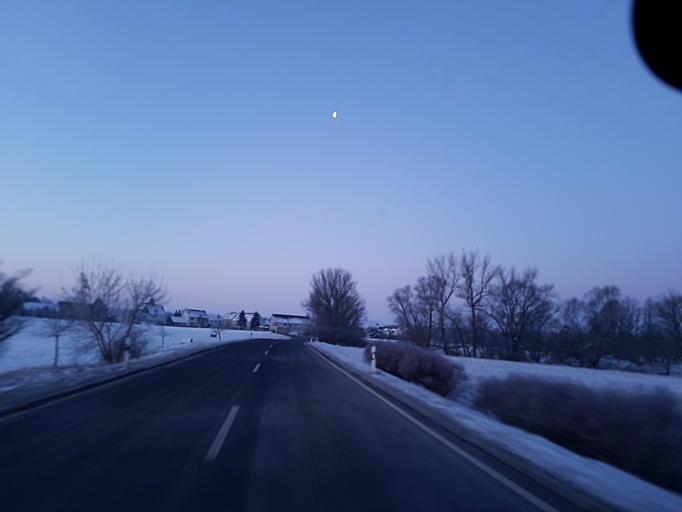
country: DE
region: Brandenburg
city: Muhlberg
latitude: 51.4233
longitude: 13.1839
